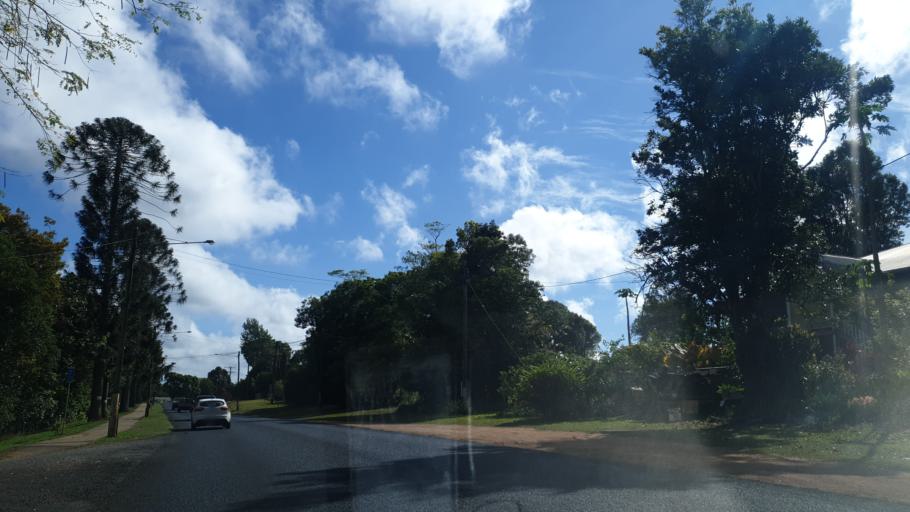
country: AU
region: Queensland
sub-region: Tablelands
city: Atherton
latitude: -17.3540
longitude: 145.5881
